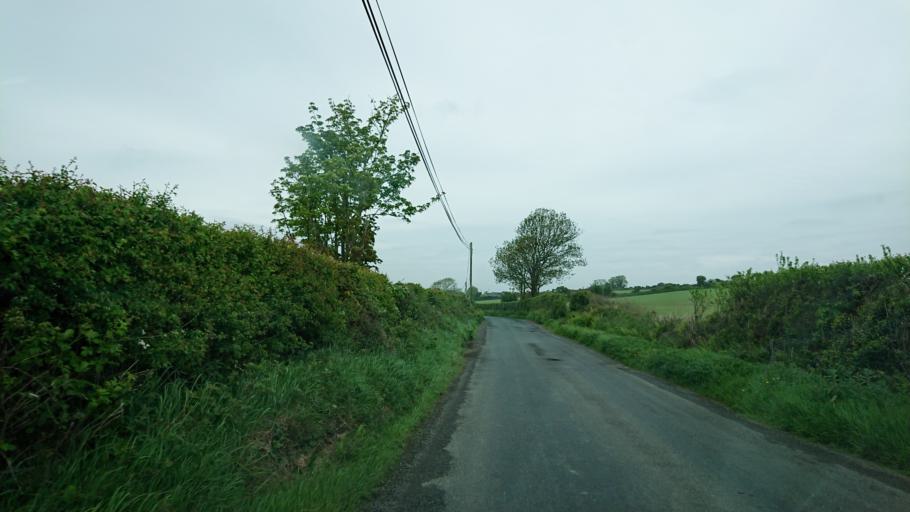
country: IE
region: Munster
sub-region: Waterford
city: Dunmore East
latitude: 52.2183
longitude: -7.0344
